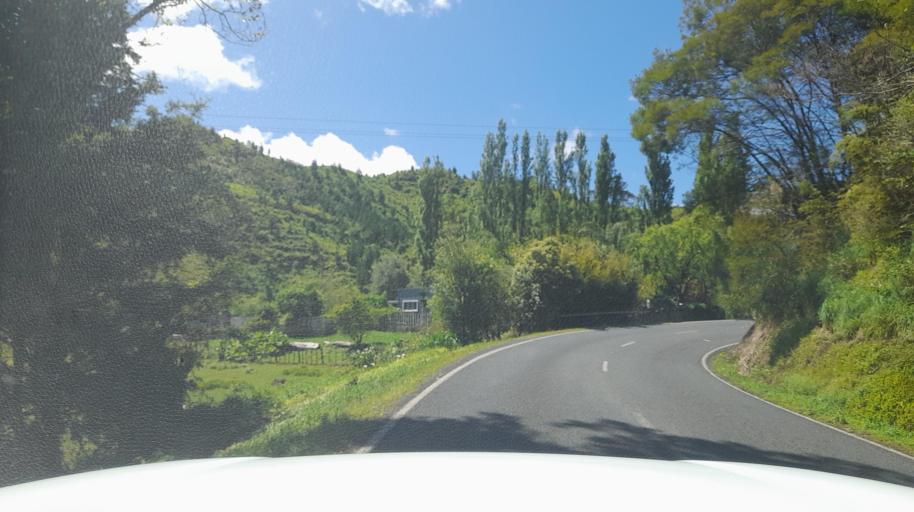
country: NZ
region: Northland
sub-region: Far North District
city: Taipa
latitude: -35.1053
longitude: 173.4062
